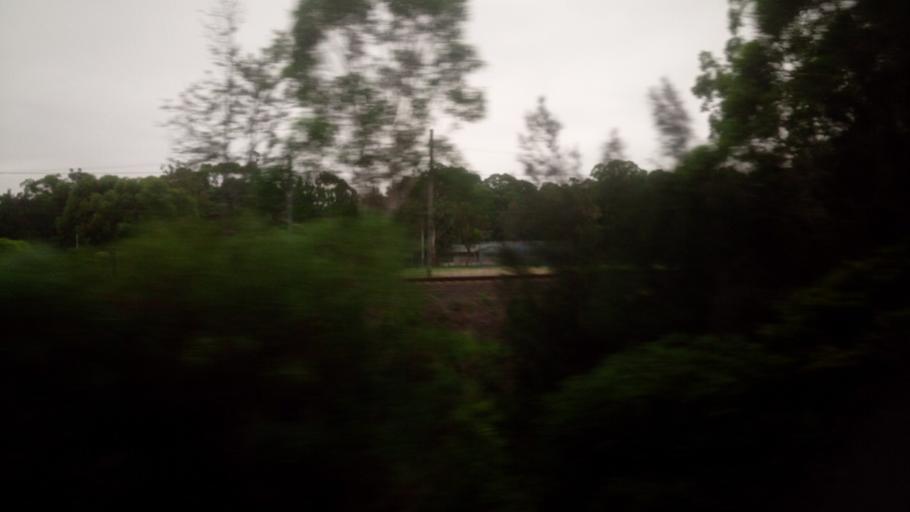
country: AU
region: New South Wales
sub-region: Blacktown
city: Blacktown
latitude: -33.7743
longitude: 150.9230
